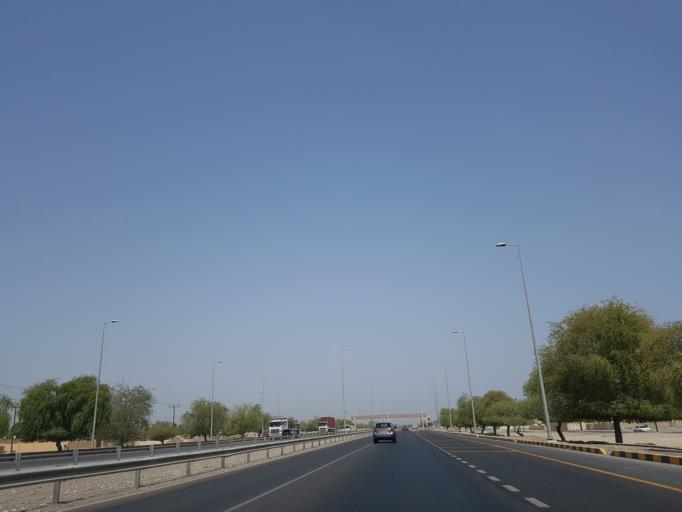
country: OM
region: Al Batinah
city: Saham
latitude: 24.0650
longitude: 56.9574
